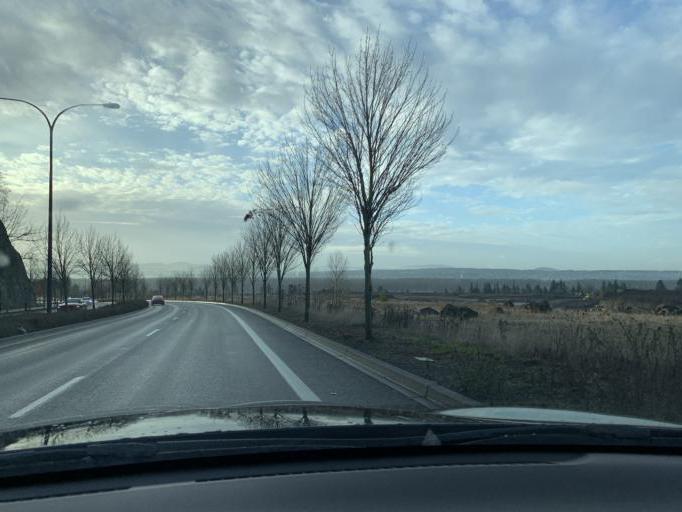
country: US
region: Washington
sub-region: Clark County
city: Mill Plain
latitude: 45.5912
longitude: -122.4754
